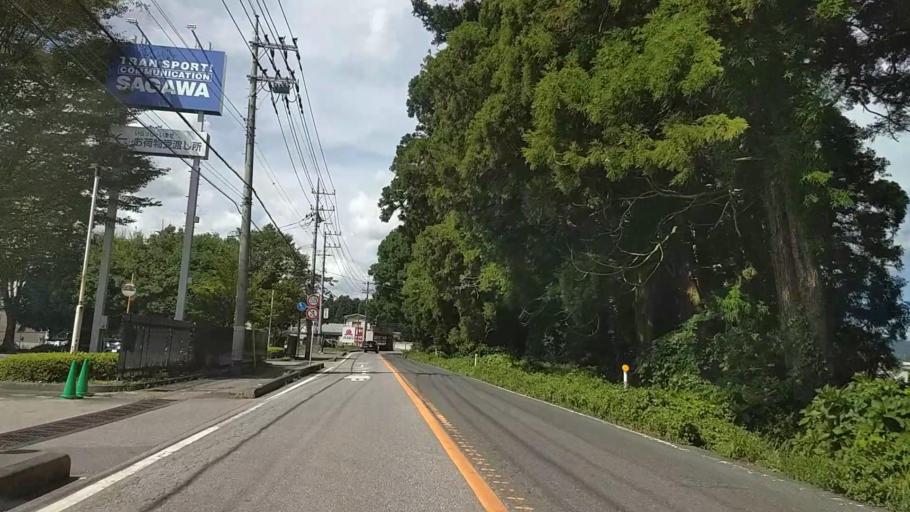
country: JP
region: Tochigi
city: Imaichi
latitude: 36.7178
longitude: 139.7134
